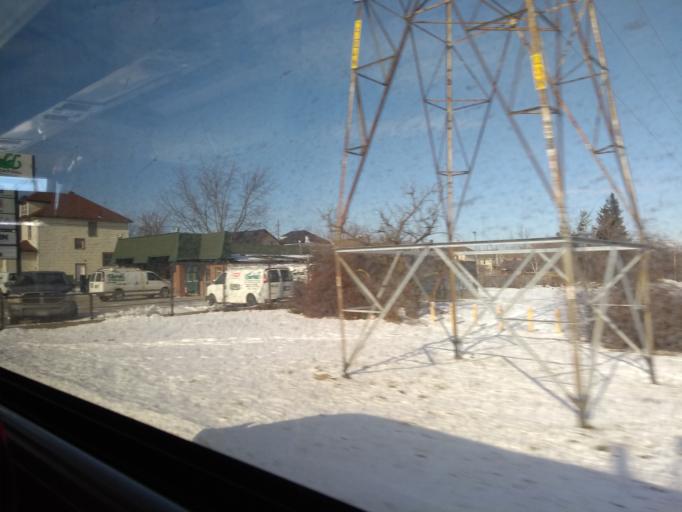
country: CA
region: Ontario
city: Niagara Falls
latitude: 43.1086
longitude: -79.0823
